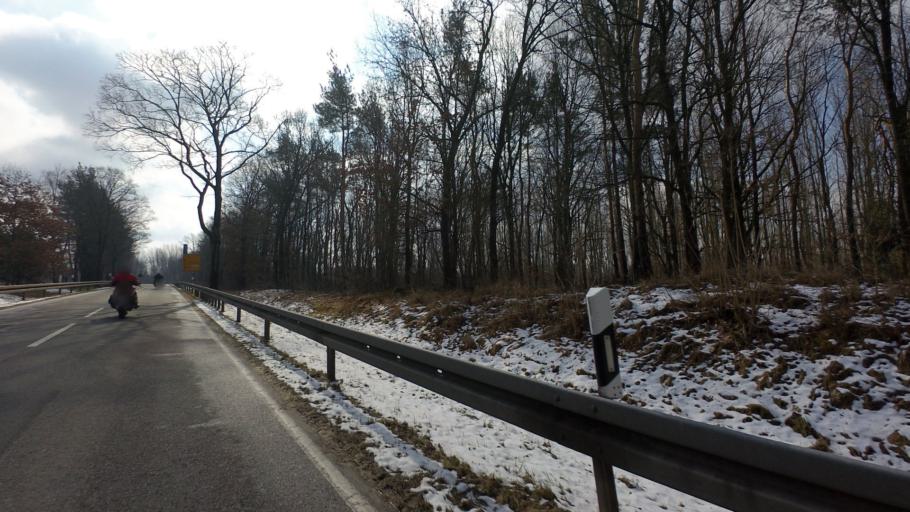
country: DE
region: Berlin
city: Buch
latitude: 52.6783
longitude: 13.5016
